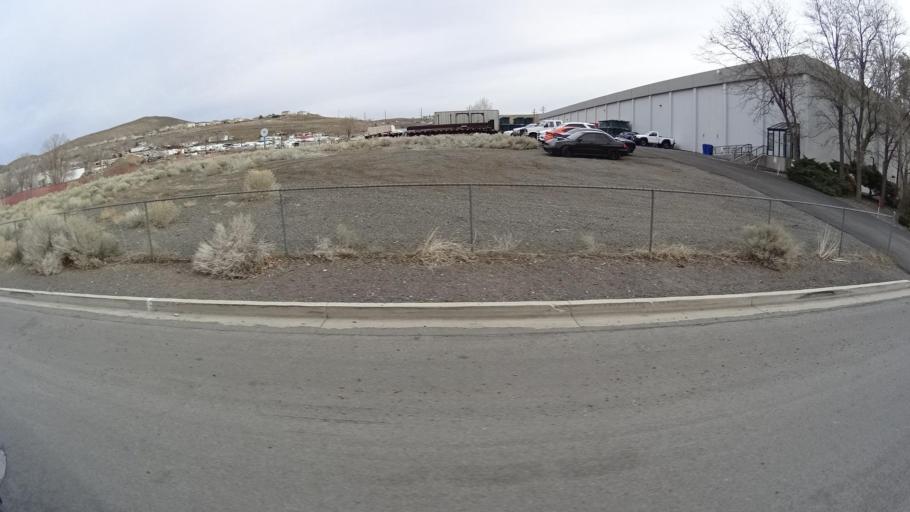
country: US
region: Nevada
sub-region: Washoe County
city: Reno
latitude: 39.5722
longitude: -119.8176
